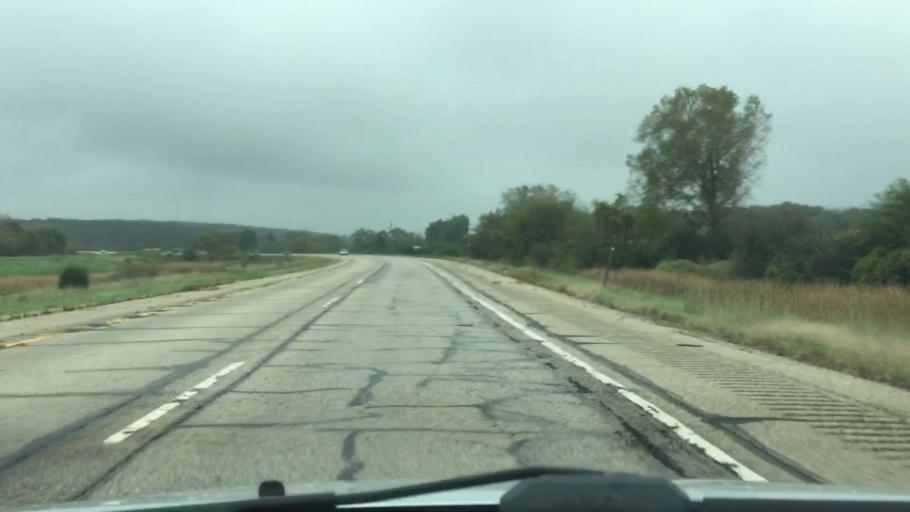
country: US
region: Wisconsin
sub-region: Walworth County
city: Como
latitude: 42.6195
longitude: -88.4609
